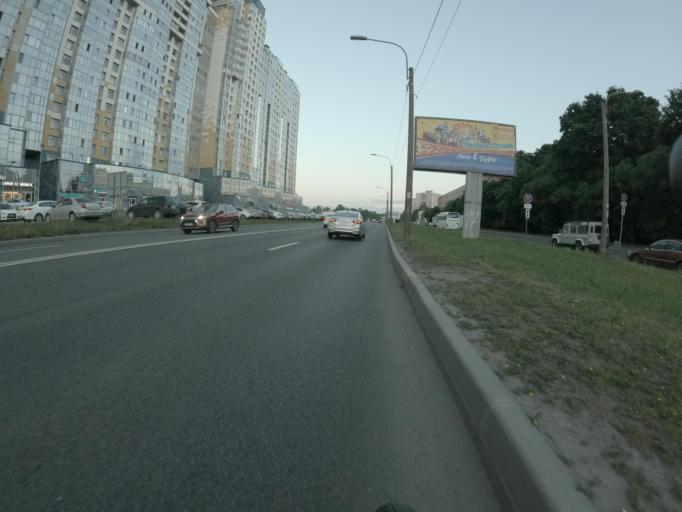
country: RU
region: St.-Petersburg
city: Avtovo
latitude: 59.8506
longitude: 30.2804
